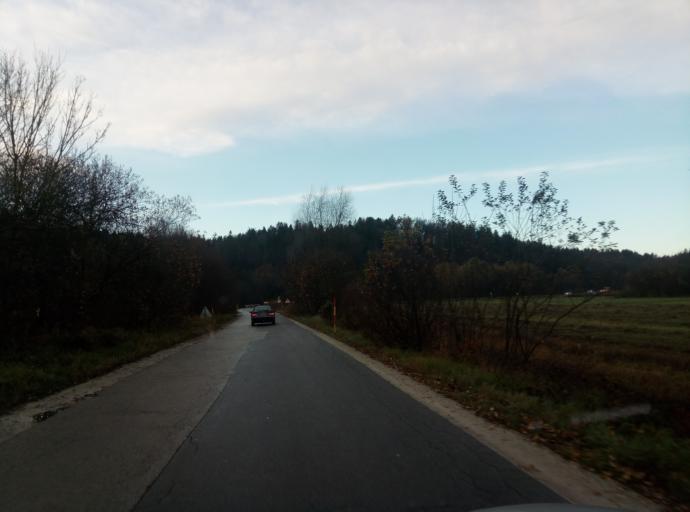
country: SI
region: Menges
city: Menges
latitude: 46.1735
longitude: 14.5625
